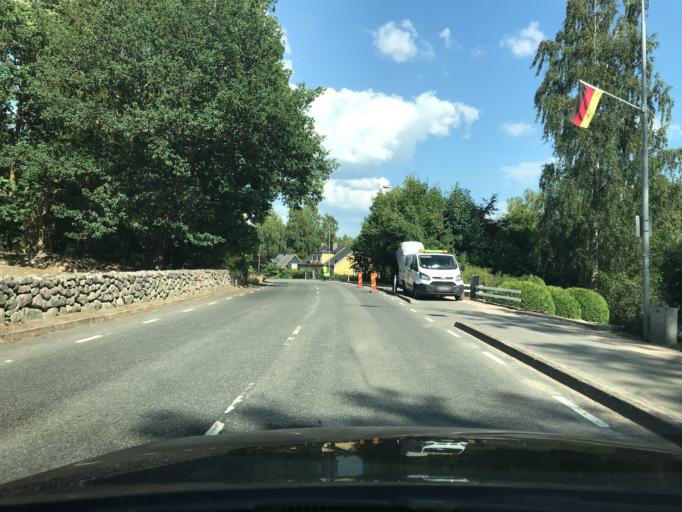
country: SE
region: Skane
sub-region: Hassleholms Kommun
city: Hastveda
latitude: 56.2860
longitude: 13.9252
